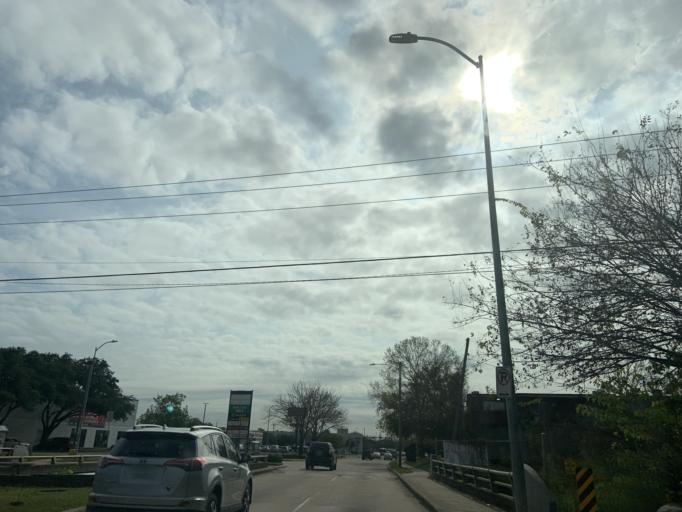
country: US
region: Texas
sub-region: Harris County
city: Bellaire
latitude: 29.6891
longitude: -95.5091
